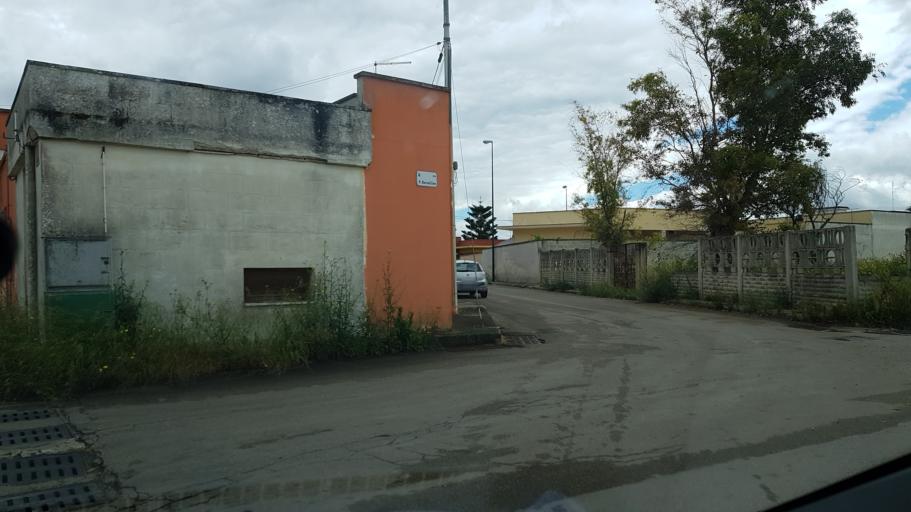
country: IT
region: Apulia
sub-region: Provincia di Brindisi
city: Torchiarolo
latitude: 40.4891
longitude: 18.0482
